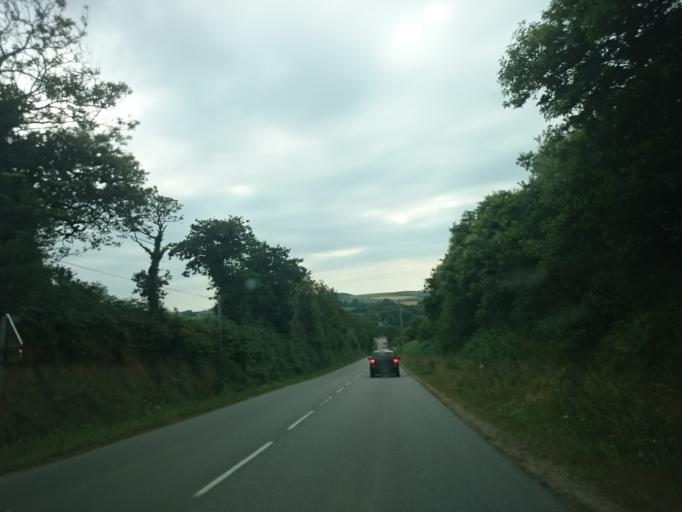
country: FR
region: Brittany
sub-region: Departement du Finistere
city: Saint-Renan
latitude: 48.4158
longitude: -4.6442
